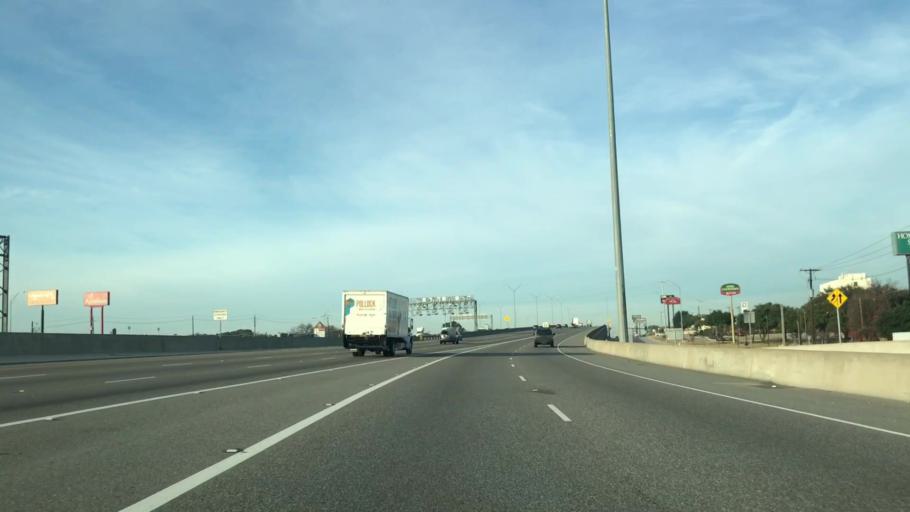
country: US
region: Texas
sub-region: Tarrant County
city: Bedford
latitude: 32.8373
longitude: -97.1278
